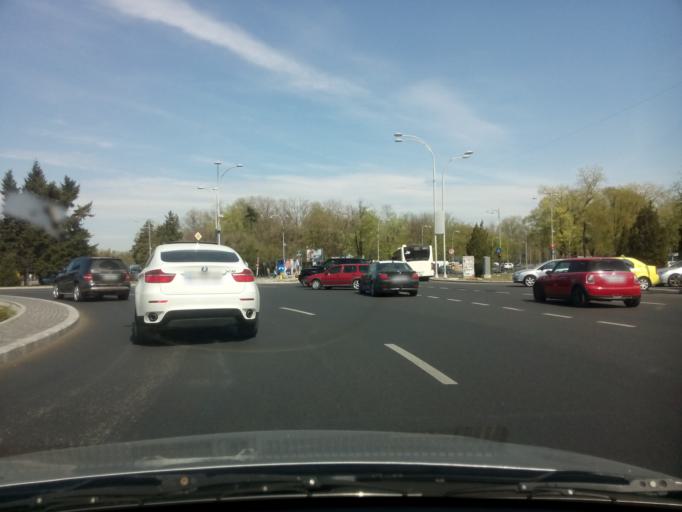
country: RO
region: Bucuresti
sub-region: Municipiul Bucuresti
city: Bucharest
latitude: 44.4662
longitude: 26.0869
